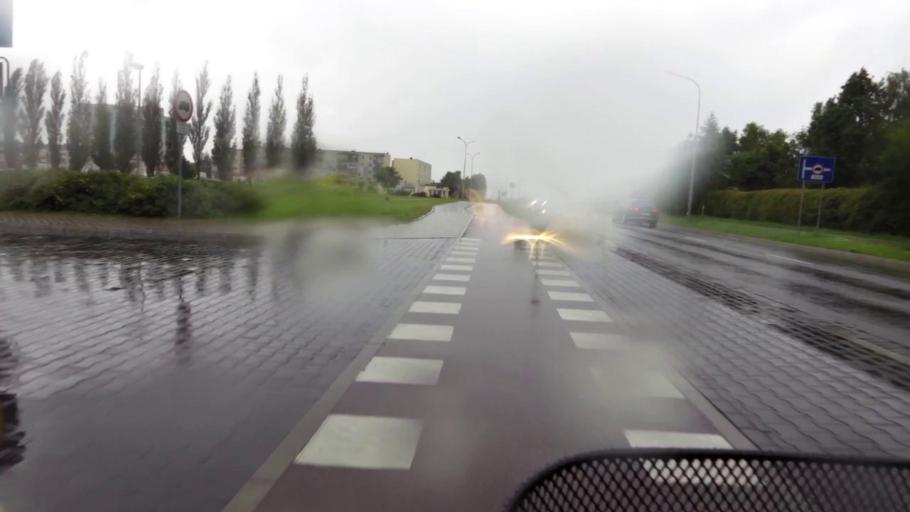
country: PL
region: West Pomeranian Voivodeship
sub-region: Koszalin
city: Koszalin
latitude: 54.2090
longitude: 16.2068
